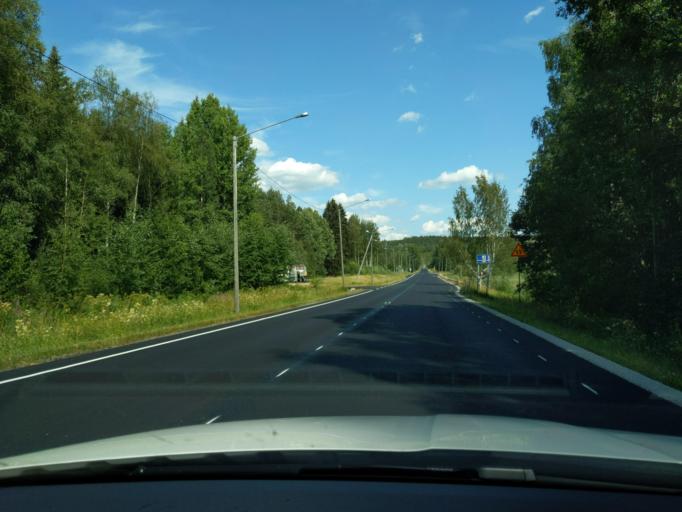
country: FI
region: Paijanne Tavastia
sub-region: Lahti
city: Nastola
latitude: 61.0709
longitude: 25.8190
